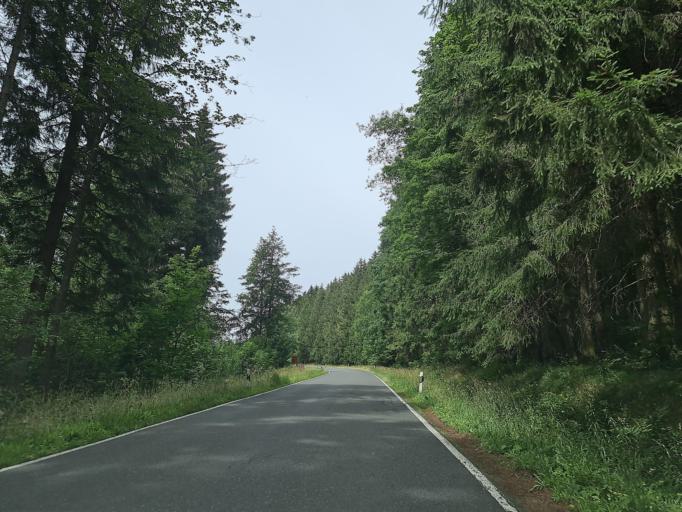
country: DE
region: Saxony
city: Sayda
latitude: 50.7036
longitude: 13.4296
